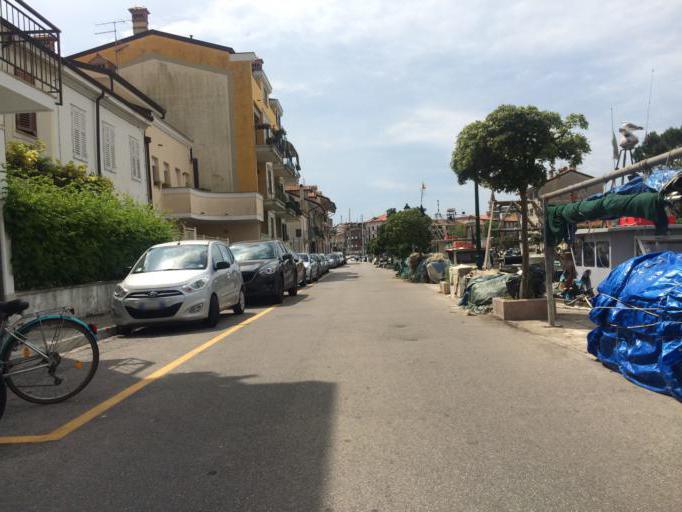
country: IT
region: Friuli Venezia Giulia
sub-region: Provincia di Gorizia
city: Grado
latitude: 45.6800
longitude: 13.3858
